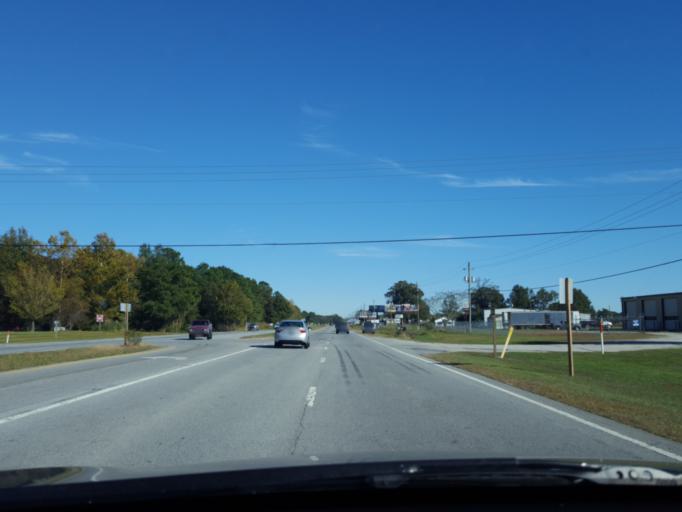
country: US
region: North Carolina
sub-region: Beaufort County
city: Washington
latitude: 35.6038
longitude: -77.1350
